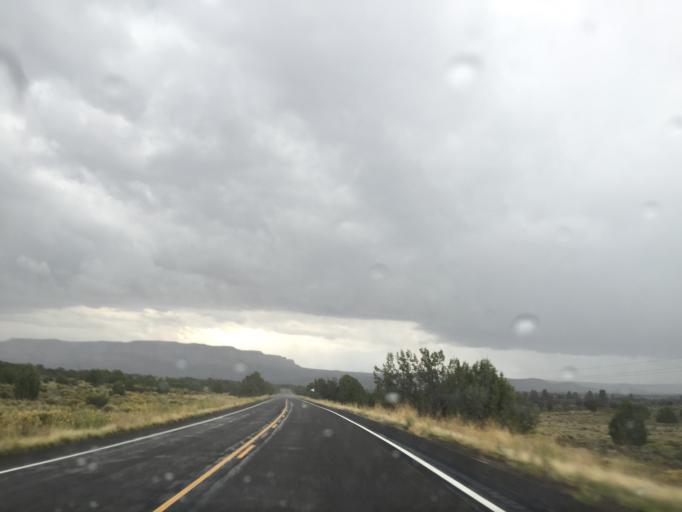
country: US
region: Utah
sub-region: Kane County
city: Kanab
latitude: 37.2265
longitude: -112.7251
